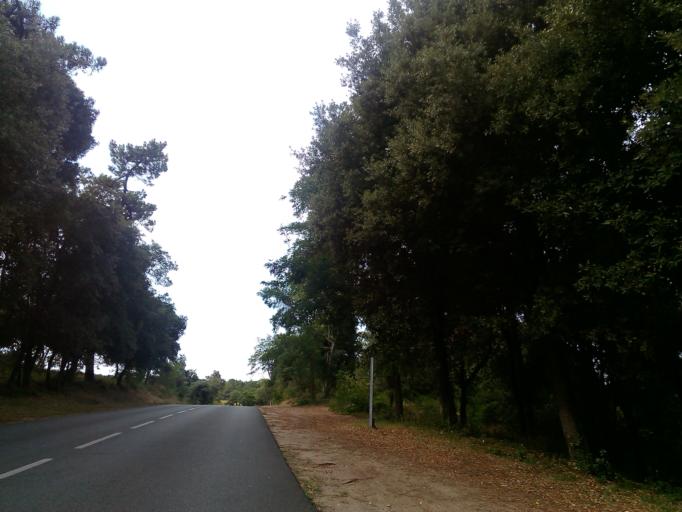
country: FR
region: Poitou-Charentes
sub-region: Departement de la Charente-Maritime
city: La Tremblade
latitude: 45.7905
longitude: -1.1835
